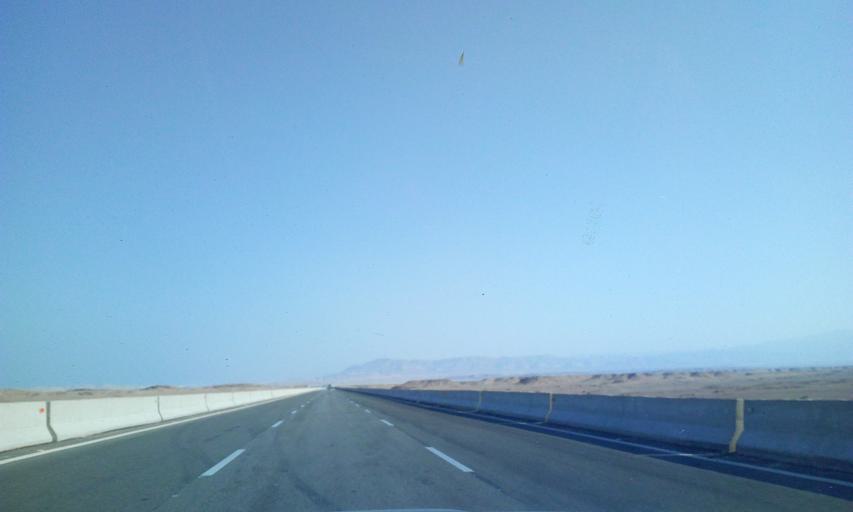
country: EG
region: As Suways
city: Ain Sukhna
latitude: 29.1522
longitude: 32.5149
